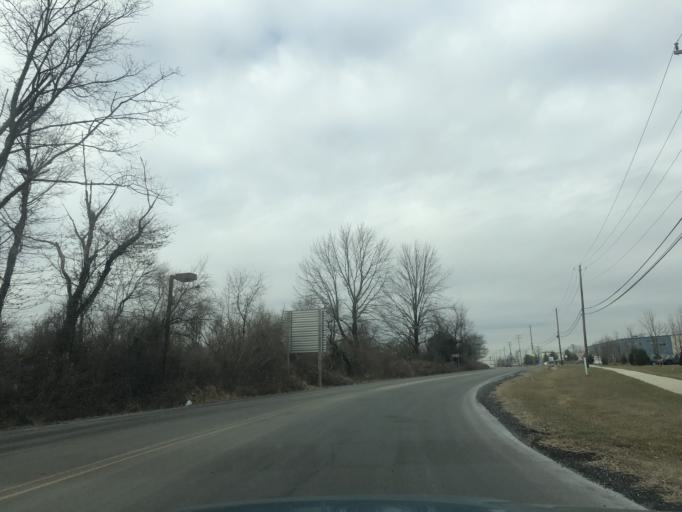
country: US
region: Pennsylvania
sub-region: Bucks County
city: Spinnerstown
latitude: 40.4369
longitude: -75.4194
